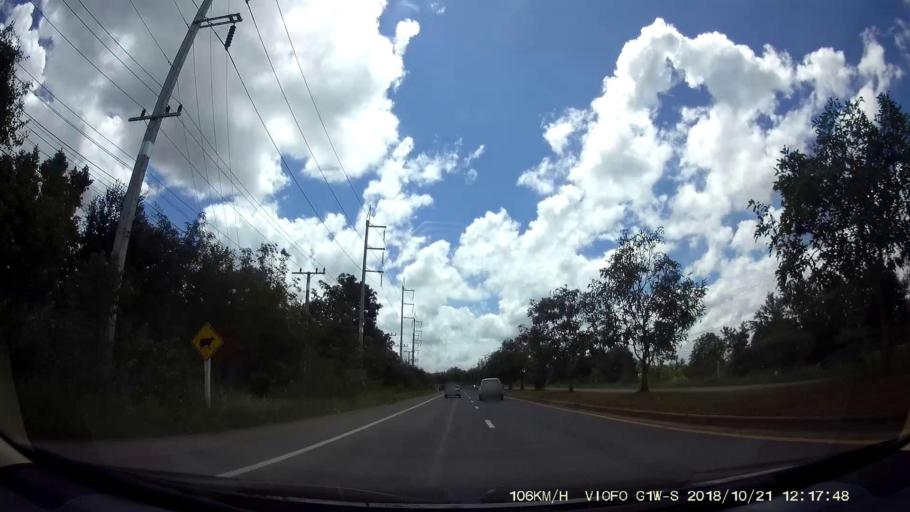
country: TH
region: Nakhon Ratchasima
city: Dan Khun Thot
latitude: 15.3261
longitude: 101.8183
